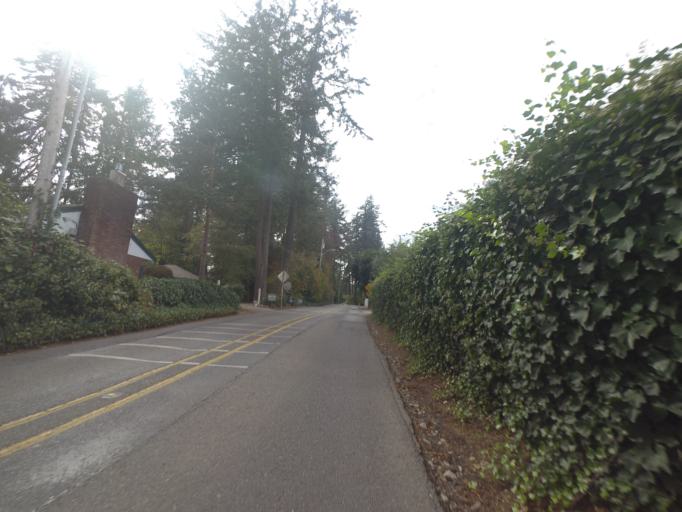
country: US
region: Washington
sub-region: Pierce County
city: Lakewood
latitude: 47.1656
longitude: -122.5423
